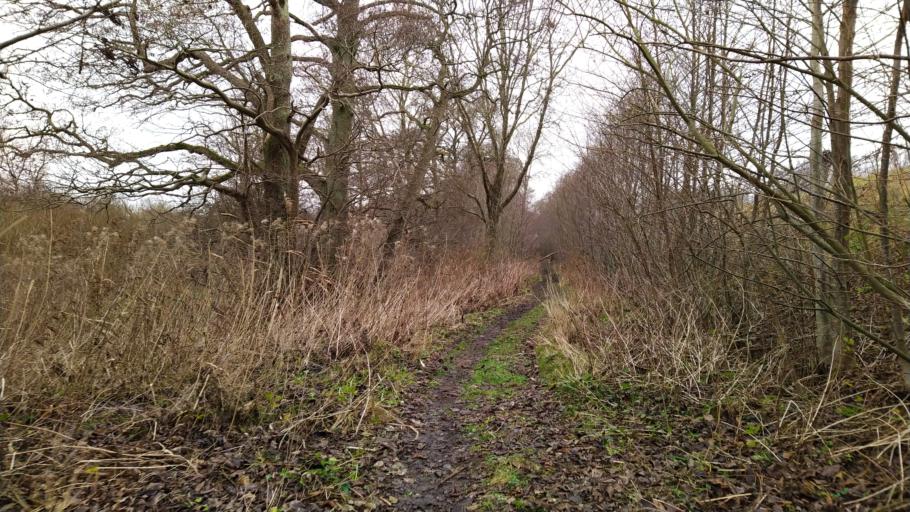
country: DK
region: Capital Region
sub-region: Egedal Kommune
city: Vekso
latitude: 55.7522
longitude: 12.2267
